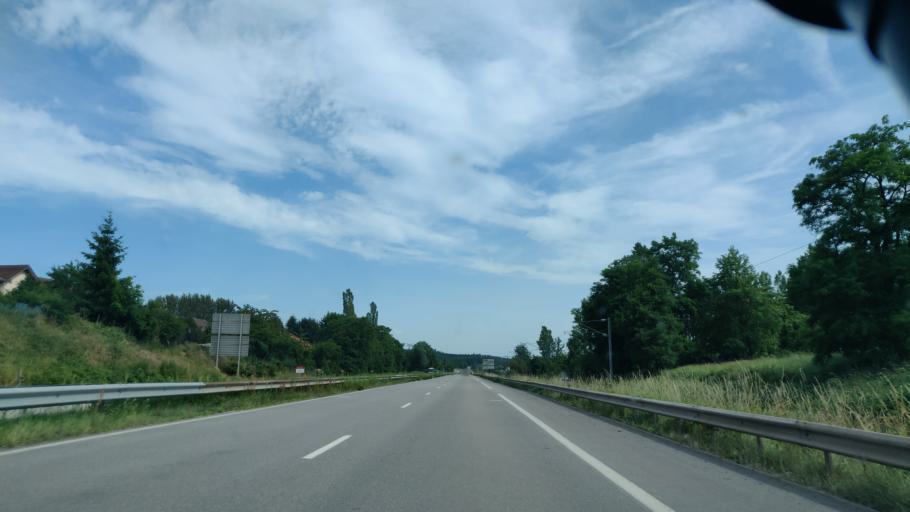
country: FR
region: Lorraine
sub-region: Departement des Vosges
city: Etival-Clairefontaine
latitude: 48.3841
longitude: 6.8684
